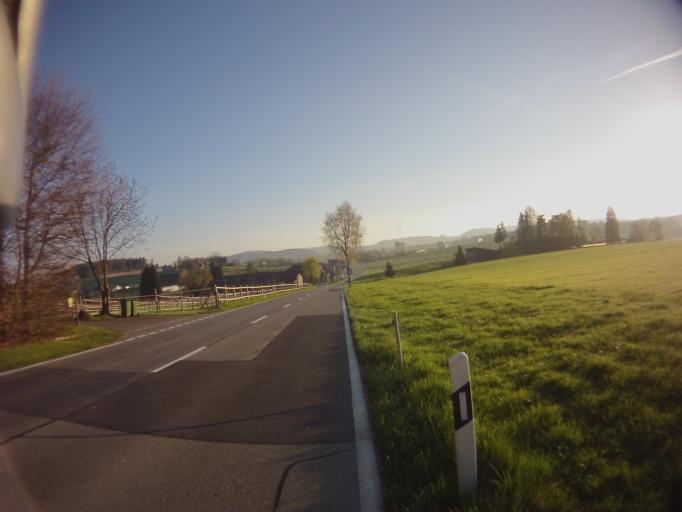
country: CH
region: Zurich
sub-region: Bezirk Affoltern
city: Knonau
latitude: 47.2062
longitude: 8.4572
